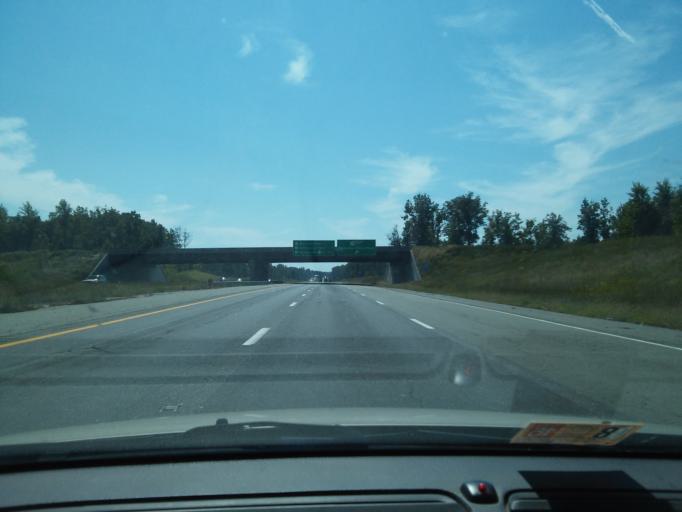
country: US
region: Virginia
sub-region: Henrico County
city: Short Pump
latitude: 37.6338
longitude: -77.6640
